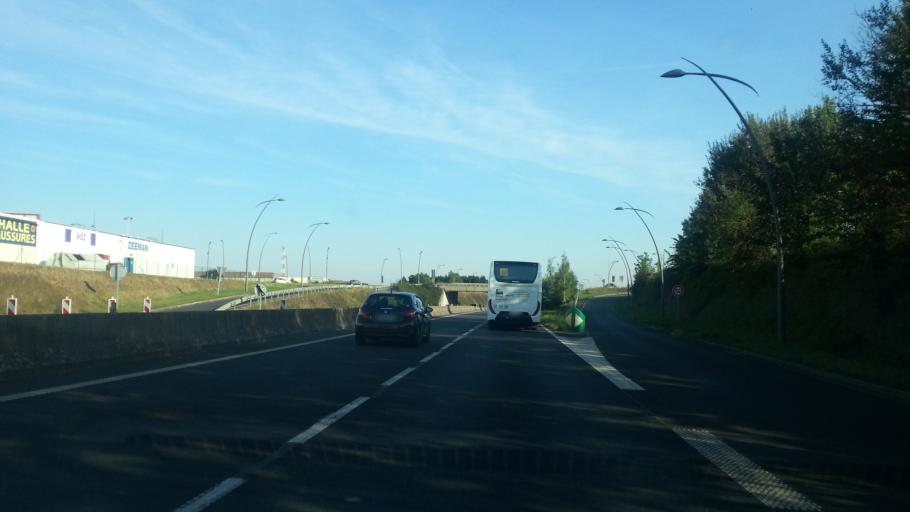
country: FR
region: Picardie
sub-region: Departement de l'Oise
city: Tille
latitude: 49.4537
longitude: 2.0969
